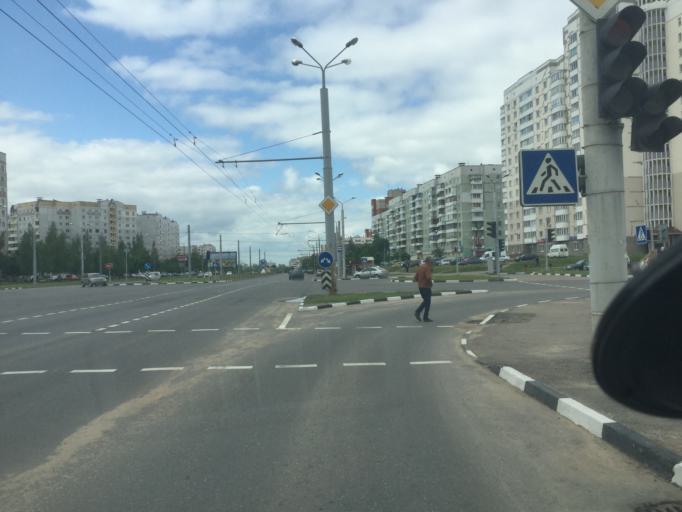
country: BY
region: Vitebsk
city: Vitebsk
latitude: 55.1618
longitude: 30.2223
